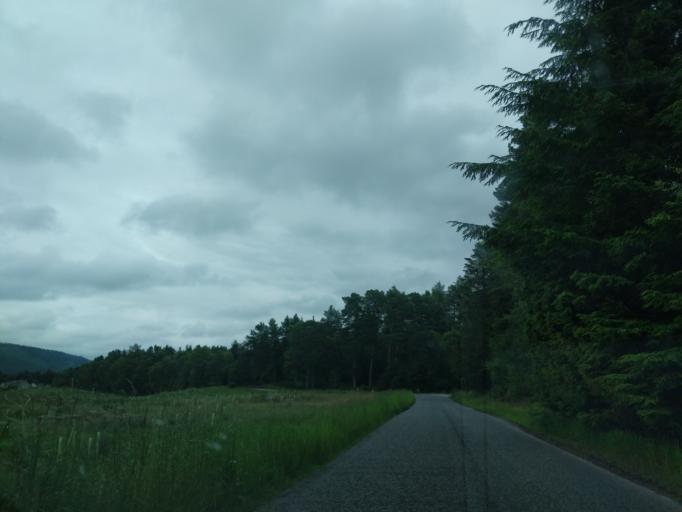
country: GB
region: Scotland
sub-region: Moray
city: Kinloss
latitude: 57.5487
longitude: -3.4777
